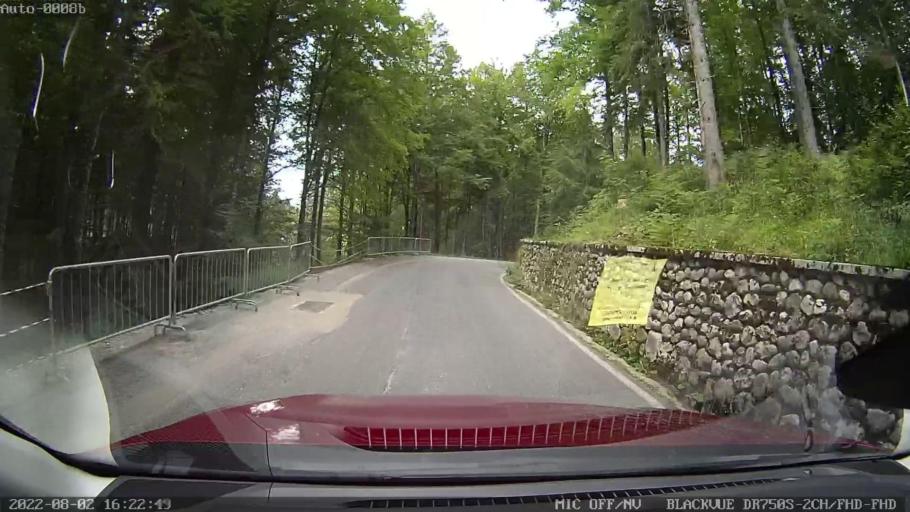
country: AT
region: Carinthia
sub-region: Politischer Bezirk Villach Land
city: Arnoldstein
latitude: 46.4749
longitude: 13.6718
